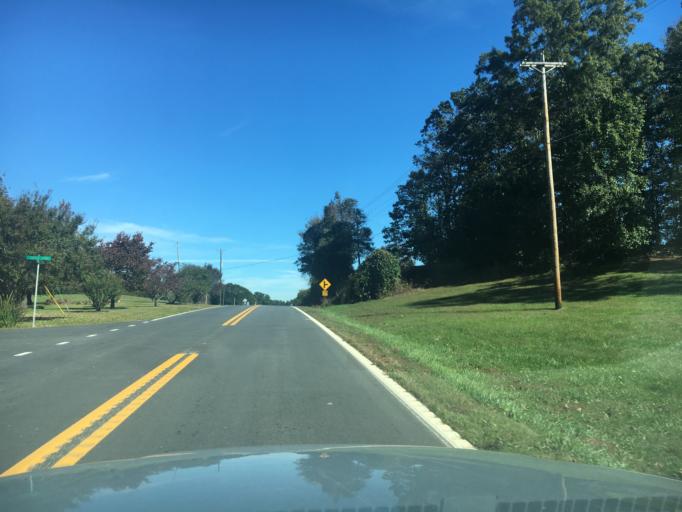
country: US
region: North Carolina
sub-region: Burke County
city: Salem
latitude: 35.6801
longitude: -81.7316
